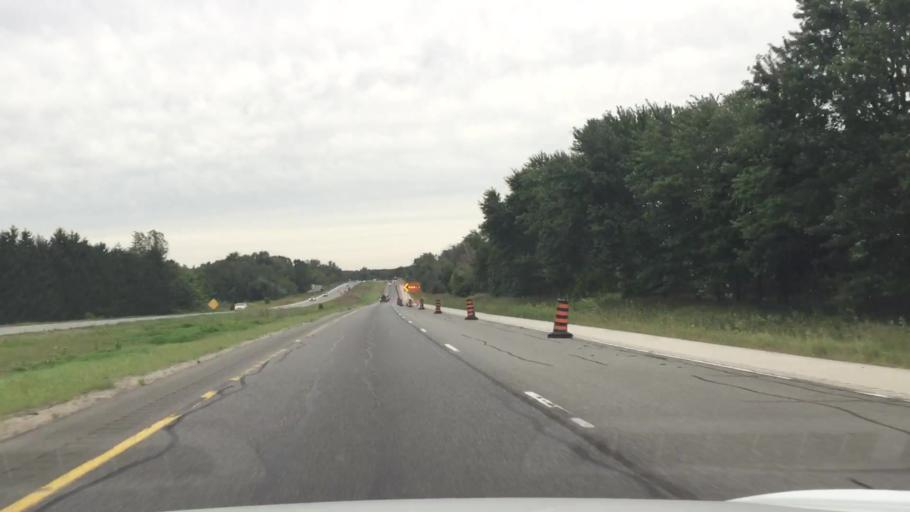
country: CA
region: Ontario
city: Delaware
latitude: 42.9346
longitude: -81.4811
